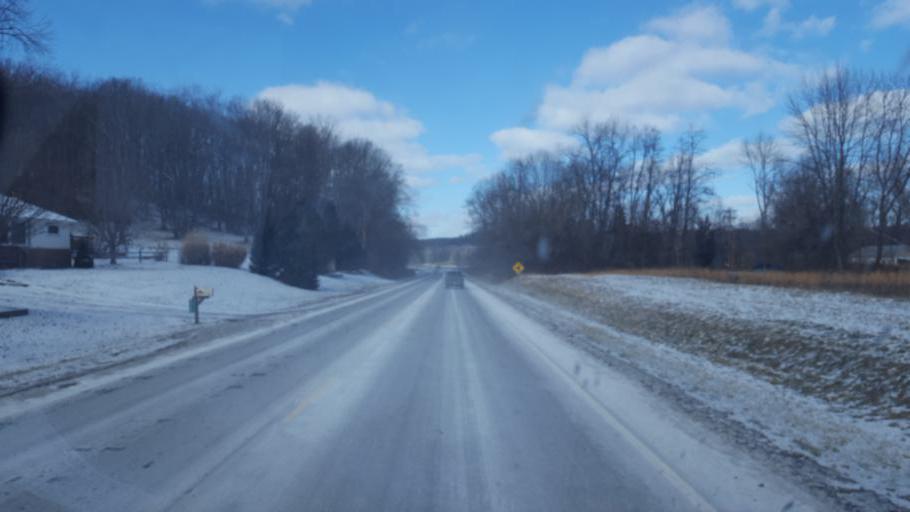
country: US
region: Ohio
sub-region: Coshocton County
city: Coshocton
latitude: 40.2992
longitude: -81.8935
